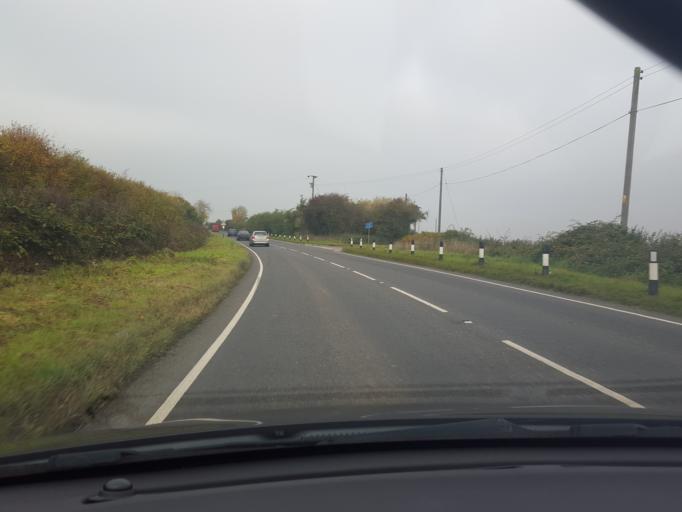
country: GB
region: England
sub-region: Essex
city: Great Bentley
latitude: 51.8346
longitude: 1.0553
